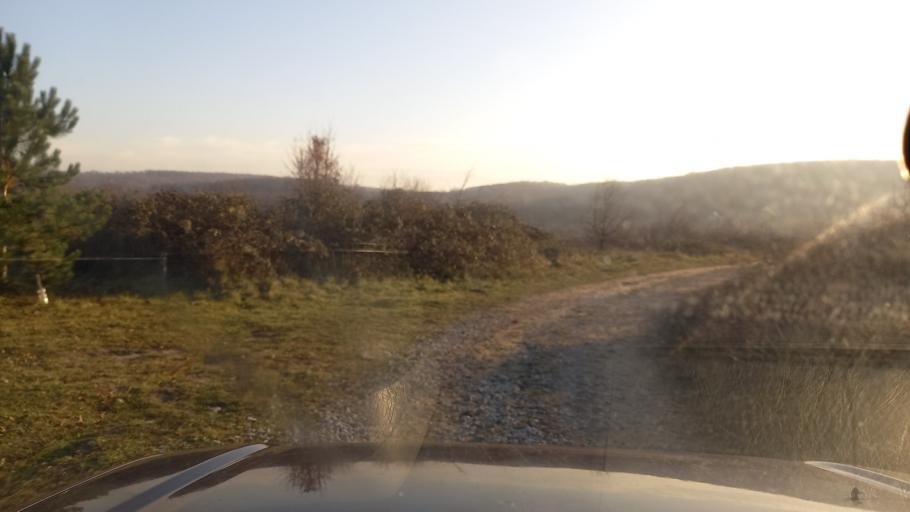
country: RU
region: Krasnodarskiy
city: Azovskaya
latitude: 44.8098
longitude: 38.5957
